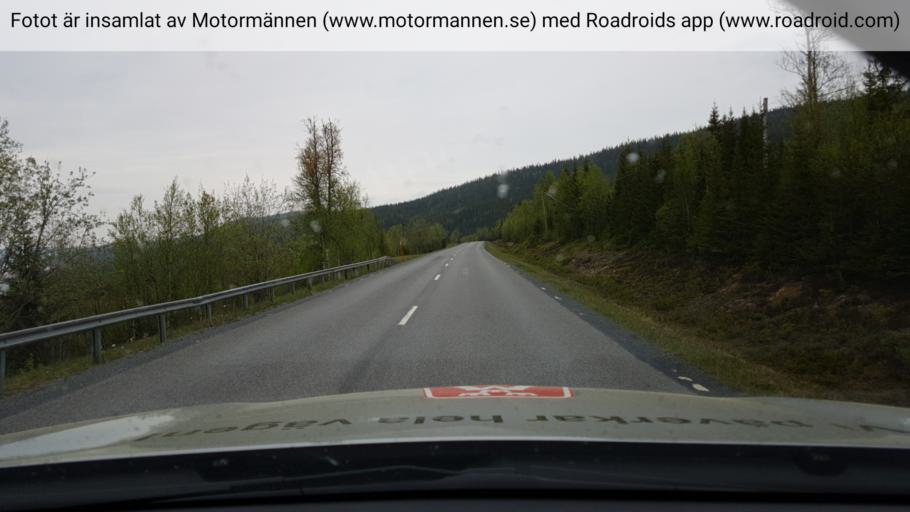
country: SE
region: Jaemtland
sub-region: Are Kommun
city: Are
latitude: 63.4887
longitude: 13.1853
